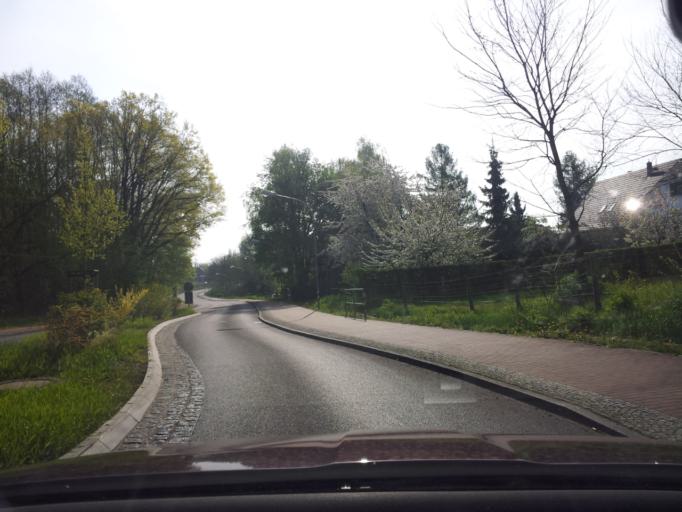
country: DE
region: Brandenburg
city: Juterbog
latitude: 51.9948
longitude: 13.0431
